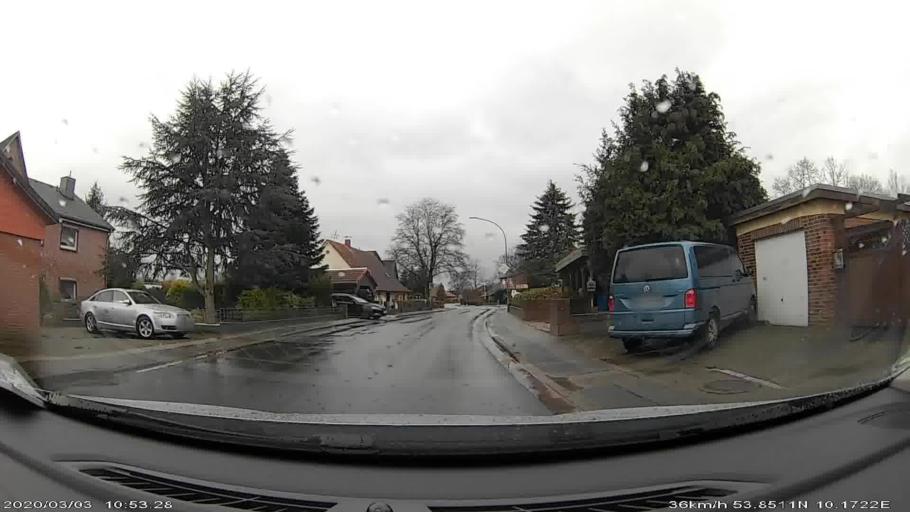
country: DE
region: Schleswig-Holstein
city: Seth
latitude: 53.8514
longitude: 10.1692
